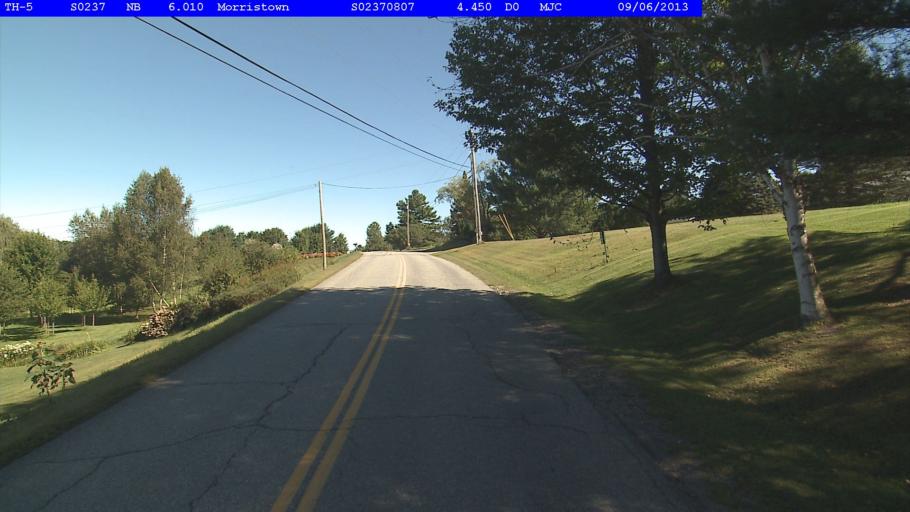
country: US
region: Vermont
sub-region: Lamoille County
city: Morristown
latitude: 44.5599
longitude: -72.6225
